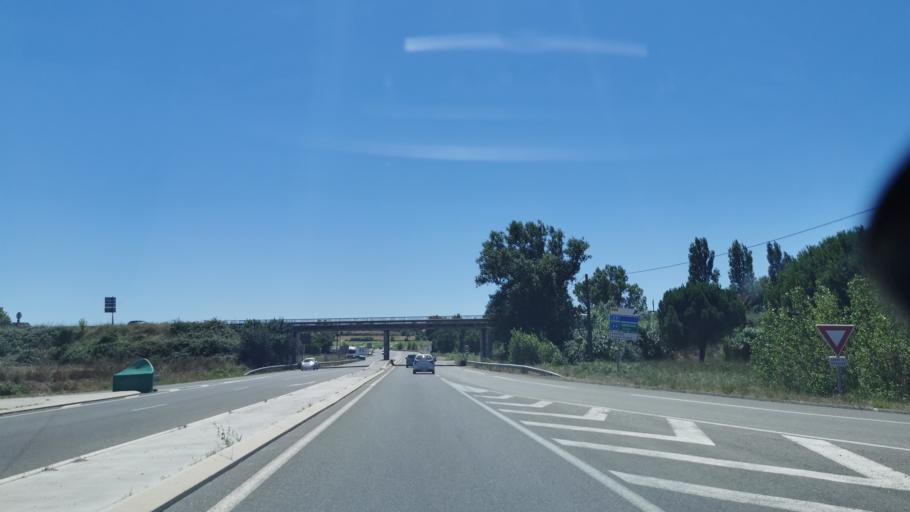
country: FR
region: Languedoc-Roussillon
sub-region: Departement de l'Herault
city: Beziers
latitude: 43.3270
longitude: 3.1921
